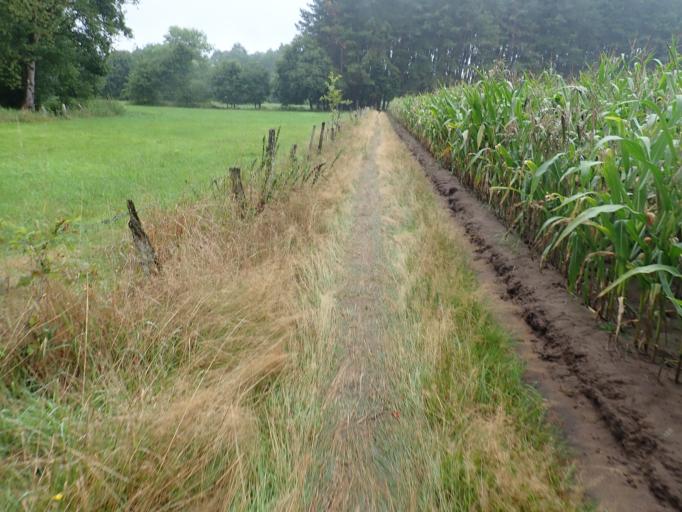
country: BE
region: Flanders
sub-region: Provincie Antwerpen
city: Lille
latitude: 51.2764
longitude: 4.8068
